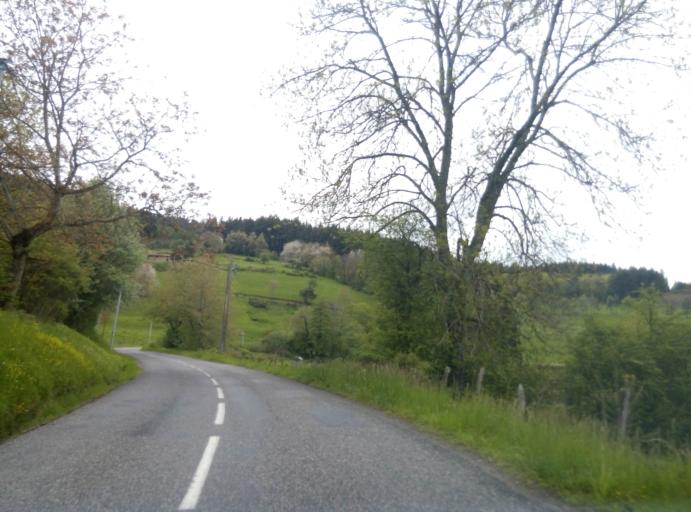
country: FR
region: Rhone-Alpes
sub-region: Departement du Rhone
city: Cublize
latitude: 45.9825
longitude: 4.4302
